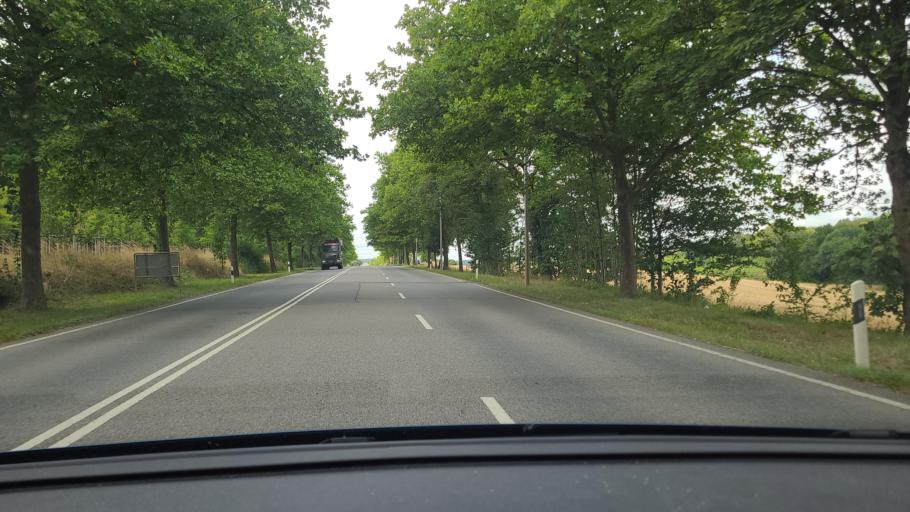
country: LU
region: Luxembourg
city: Schouweiler
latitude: 49.5740
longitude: 5.9371
